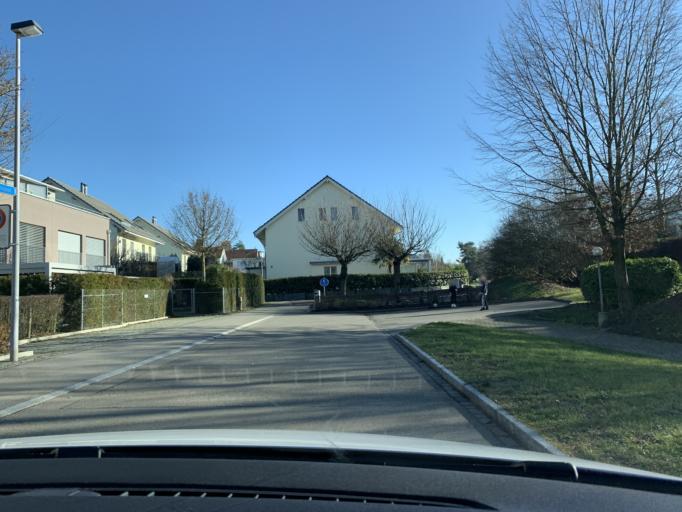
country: CH
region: Zurich
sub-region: Bezirk Dielsdorf
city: Sonnhalde
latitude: 47.4541
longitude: 8.4628
